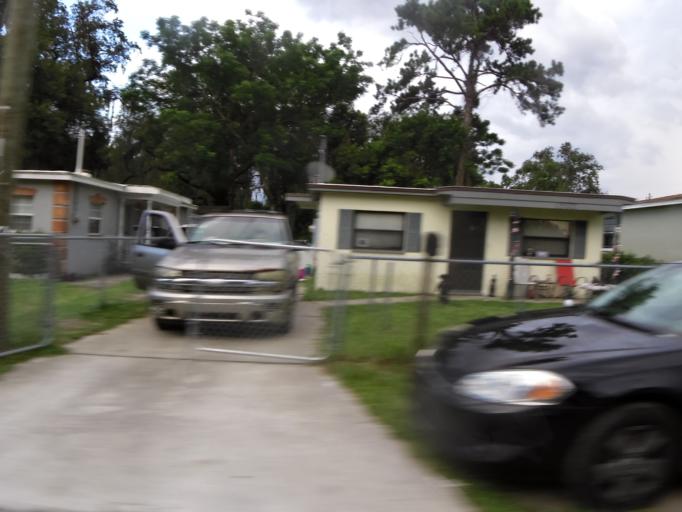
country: US
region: Florida
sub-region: Duval County
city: Jacksonville
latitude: 30.3475
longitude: -81.6354
